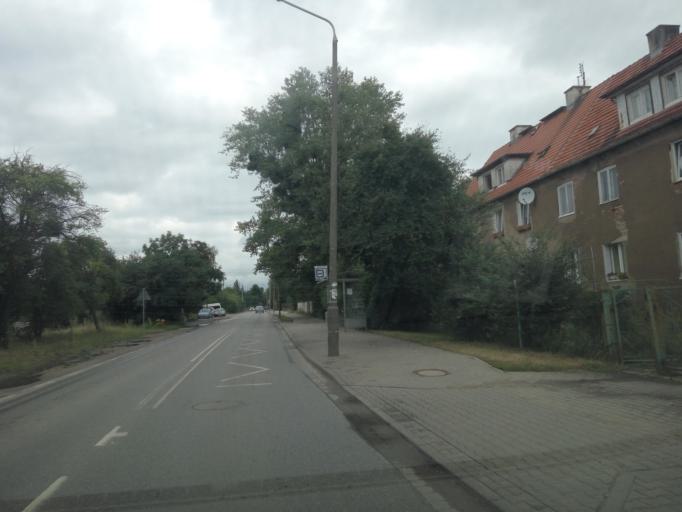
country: PL
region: Lower Silesian Voivodeship
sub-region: Powiat wroclawski
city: Zerniki Wroclawskie
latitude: 51.0503
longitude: 17.0307
